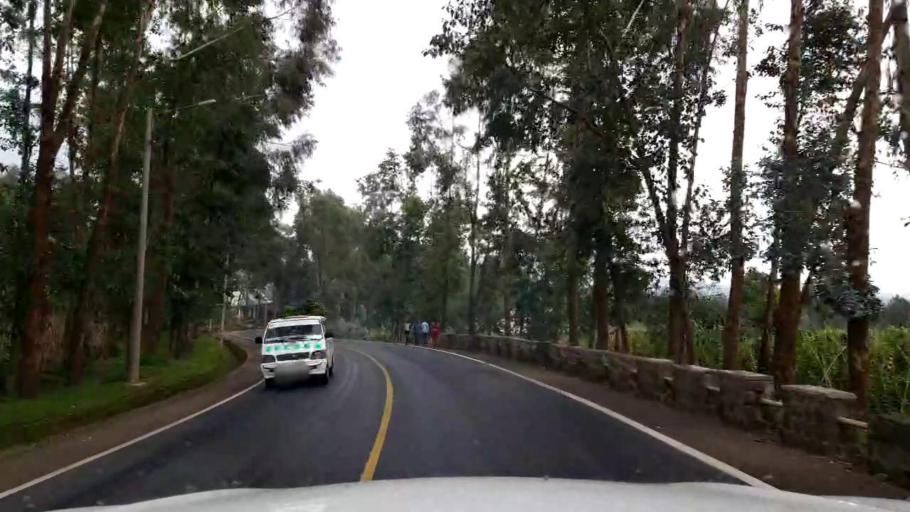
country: RW
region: Western Province
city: Gisenyi
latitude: -1.6736
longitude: 29.3571
